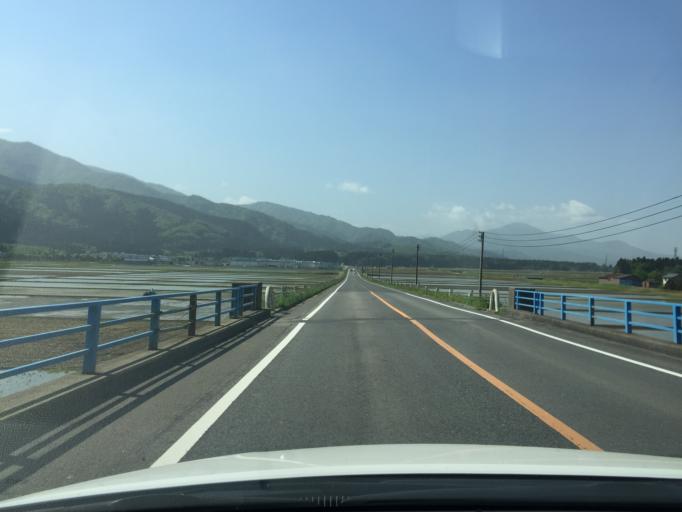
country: JP
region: Niigata
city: Gosen
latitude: 37.7299
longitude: 139.2309
